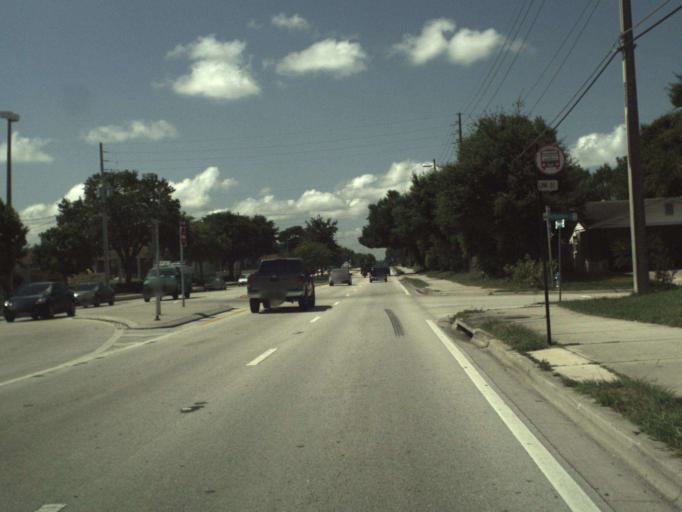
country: US
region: Florida
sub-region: Orange County
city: Conway
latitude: 28.5221
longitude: -81.3311
